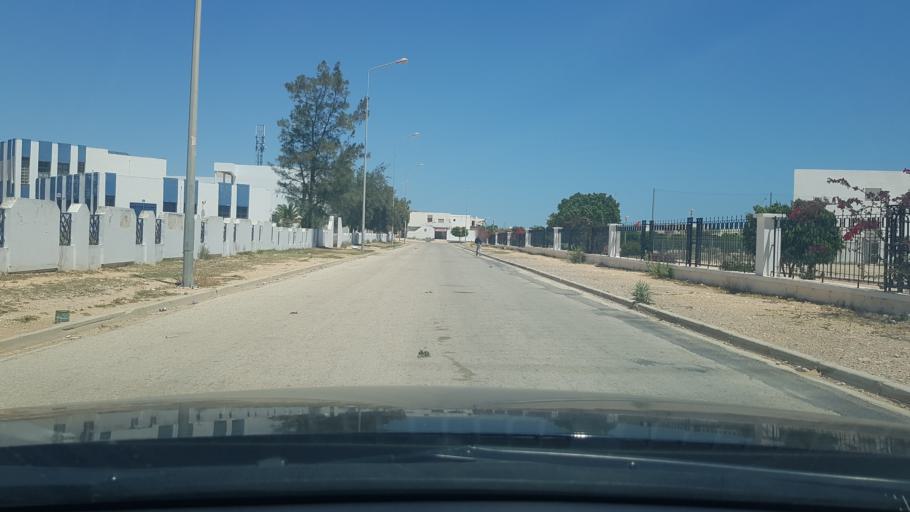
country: TN
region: Safaqis
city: Al Qarmadah
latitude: 34.8394
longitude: 10.7559
